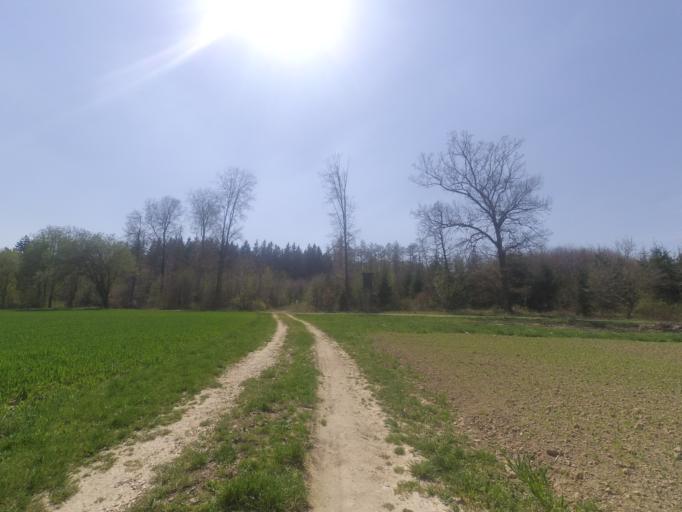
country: DE
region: Bavaria
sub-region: Swabia
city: Weissenhorn
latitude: 48.2848
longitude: 10.1873
